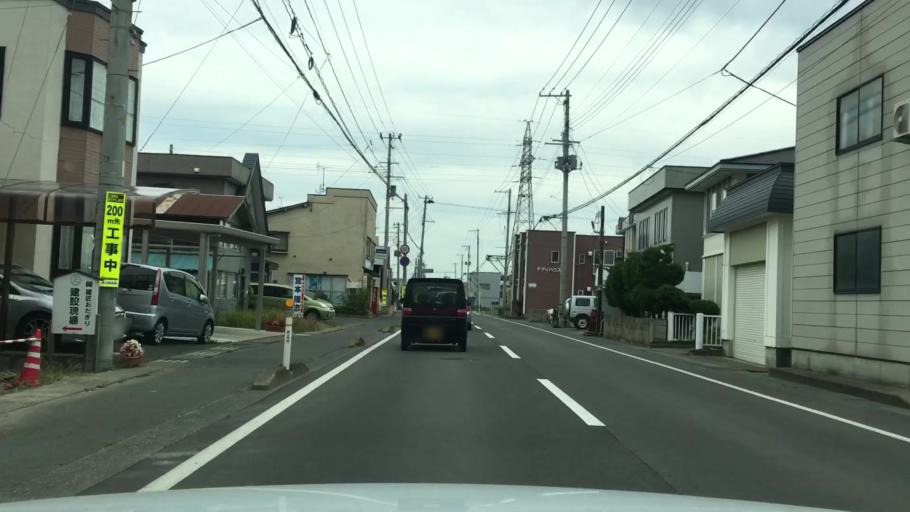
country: JP
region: Aomori
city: Hirosaki
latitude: 40.6251
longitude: 140.4560
